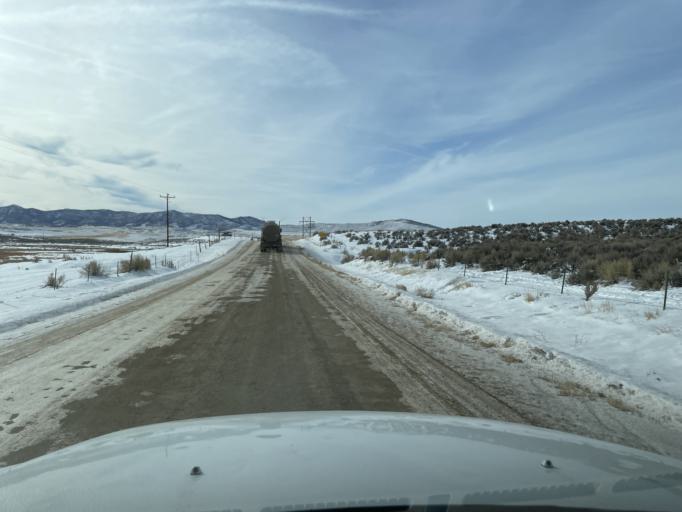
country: US
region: Colorado
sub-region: Moffat County
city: Craig
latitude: 40.3226
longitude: -107.6882
